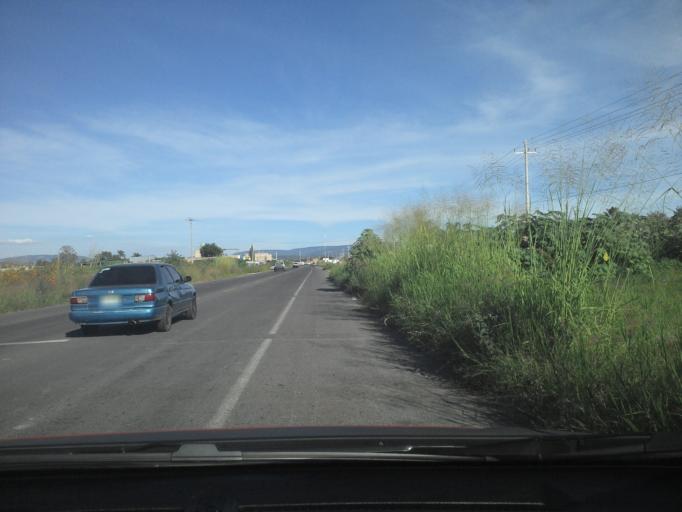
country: MX
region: Jalisco
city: El Refugio
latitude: 20.6666
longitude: -103.7440
